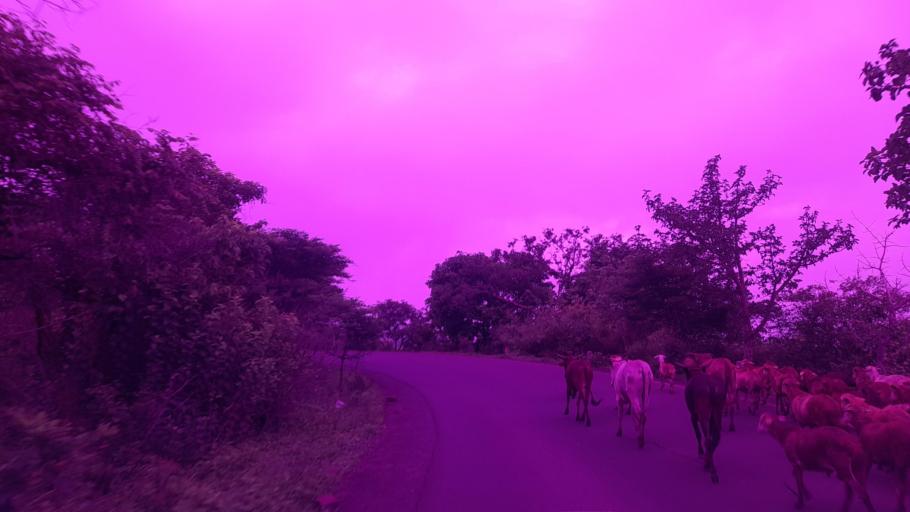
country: ET
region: Oromiya
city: Waliso
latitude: 8.1743
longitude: 37.5824
